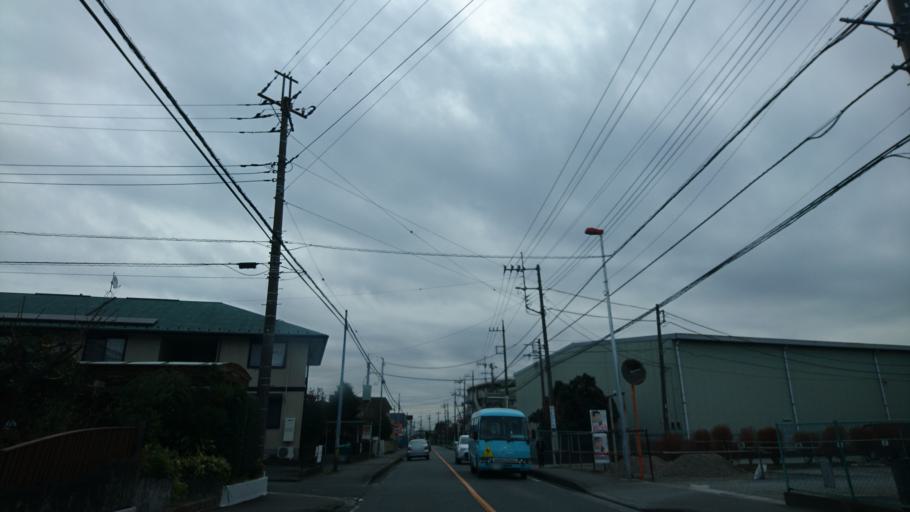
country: JP
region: Tokyo
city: Hachioji
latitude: 35.5782
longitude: 139.3347
